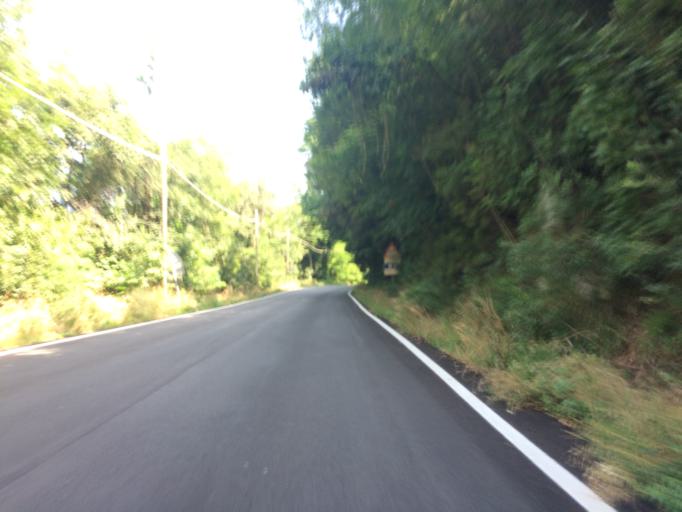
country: IT
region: Liguria
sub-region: Provincia di Savona
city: Varazze
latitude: 44.3805
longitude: 8.5682
